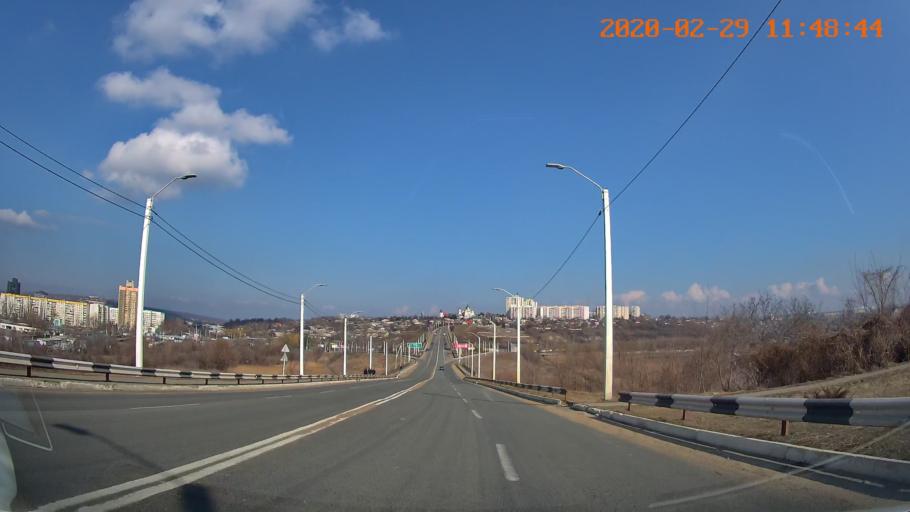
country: MD
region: Telenesti
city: Ribnita
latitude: 47.7499
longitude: 28.9921
